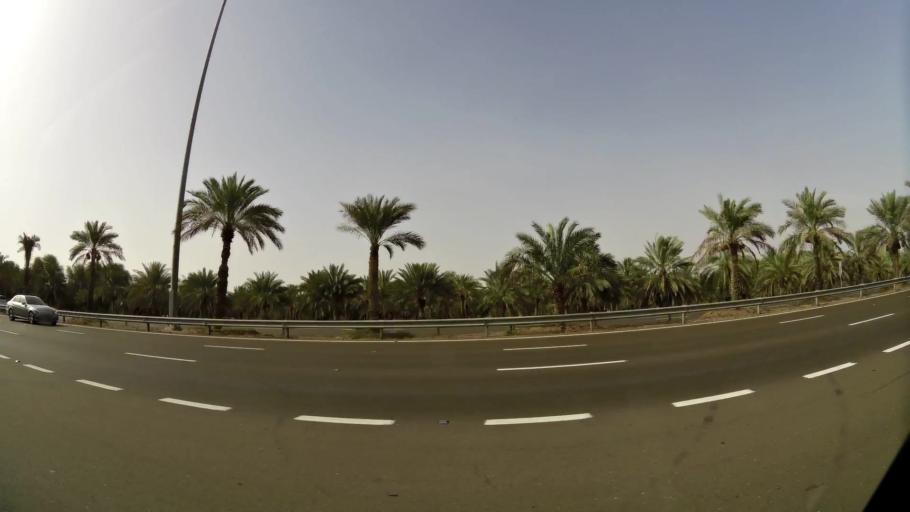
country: AE
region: Abu Dhabi
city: Al Ain
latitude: 24.2011
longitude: 55.5818
